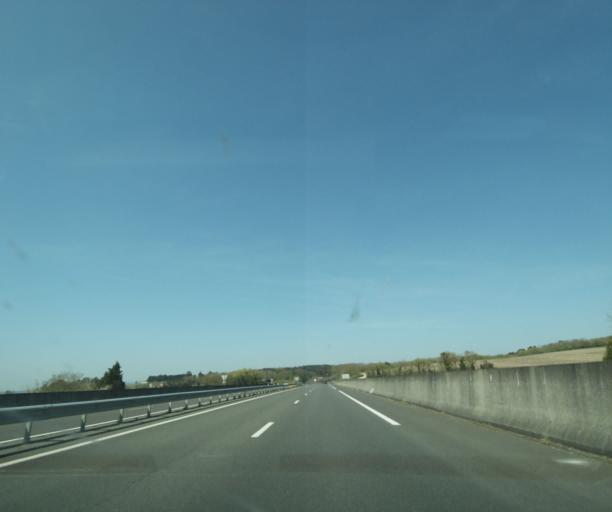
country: FR
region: Bourgogne
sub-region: Departement de la Nievre
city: Pouilly-sur-Loire
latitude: 47.2864
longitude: 2.9640
